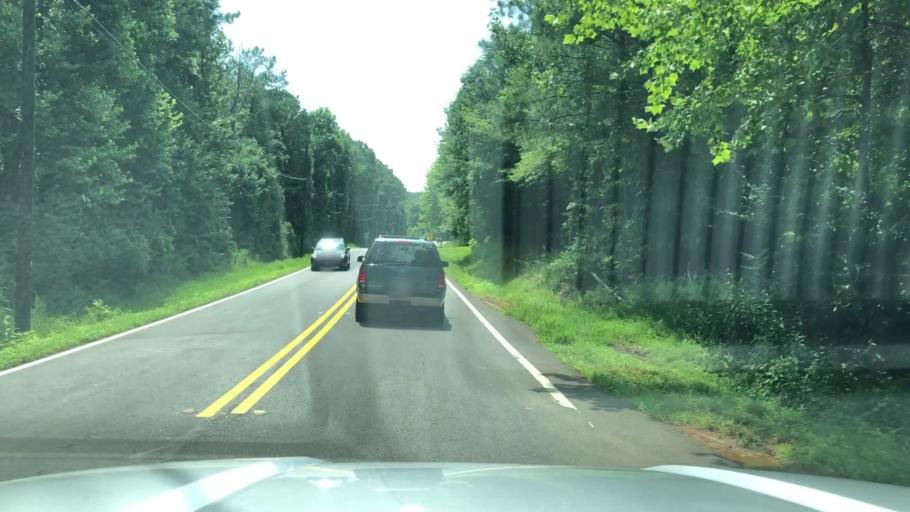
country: US
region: Georgia
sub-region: Bartow County
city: Emerson
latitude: 34.0811
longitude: -84.7581
